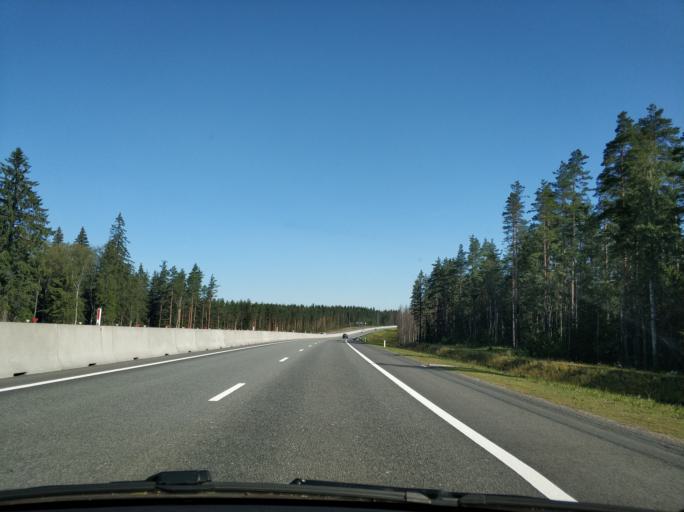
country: RU
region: Leningrad
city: Sosnovo
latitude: 60.5276
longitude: 30.1658
